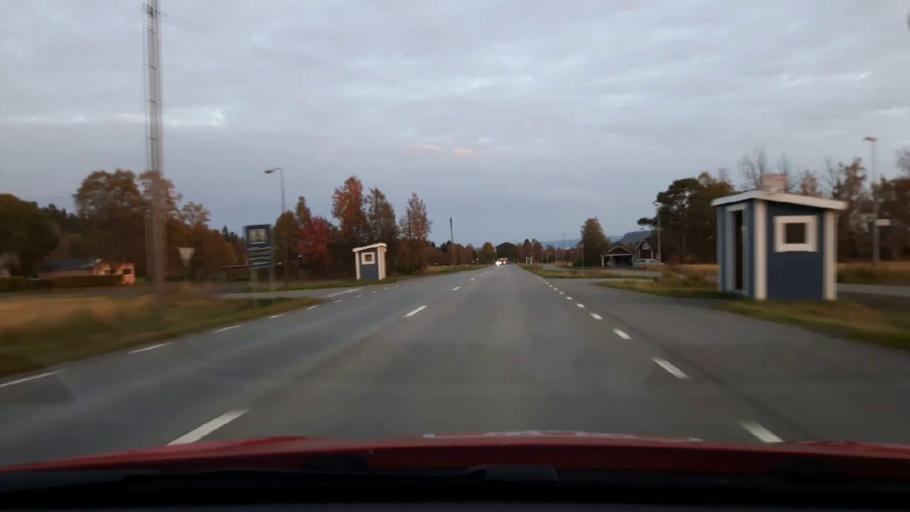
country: SE
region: Jaemtland
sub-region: OEstersunds Kommun
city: Ostersund
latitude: 63.2364
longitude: 14.5770
